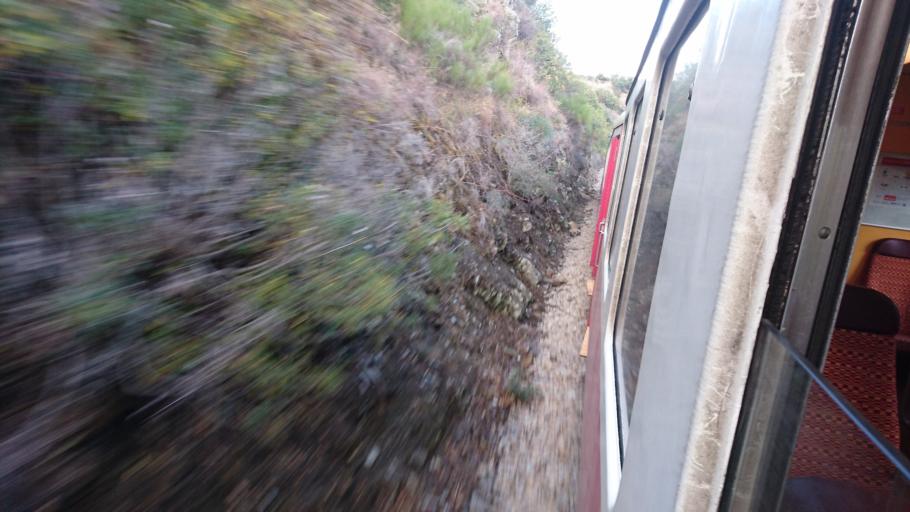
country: PT
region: Guarda
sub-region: Vila Nova de Foz Coa
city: Vila Nova de Foz Coa
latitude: 41.1241
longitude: -7.1680
